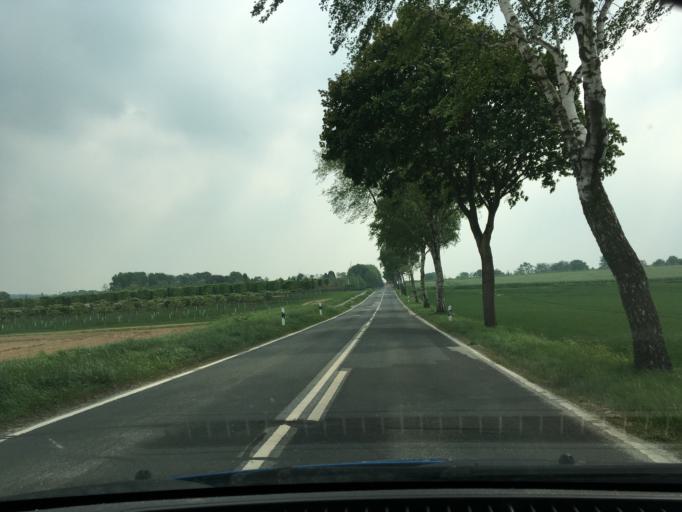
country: DE
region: Lower Saxony
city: Seevetal
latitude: 53.4135
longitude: 9.8957
